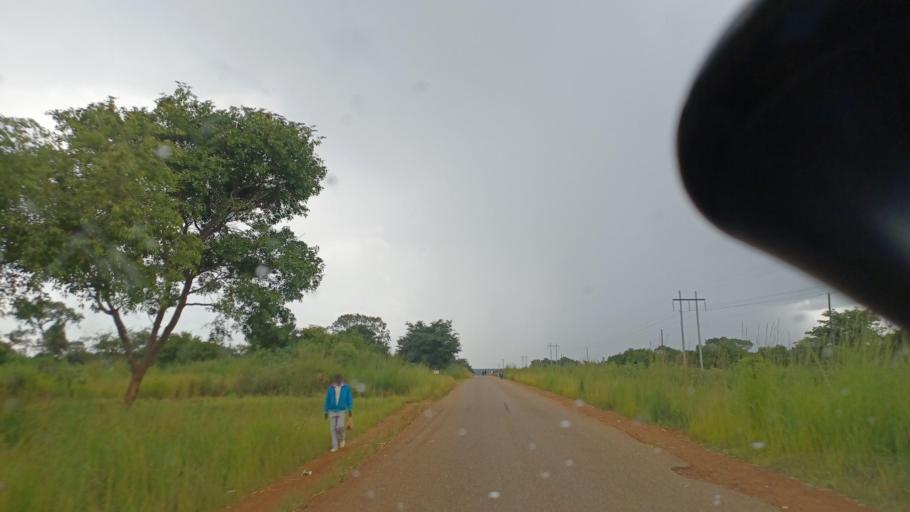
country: ZM
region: North-Western
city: Kasempa
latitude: -13.0522
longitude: 25.9882
